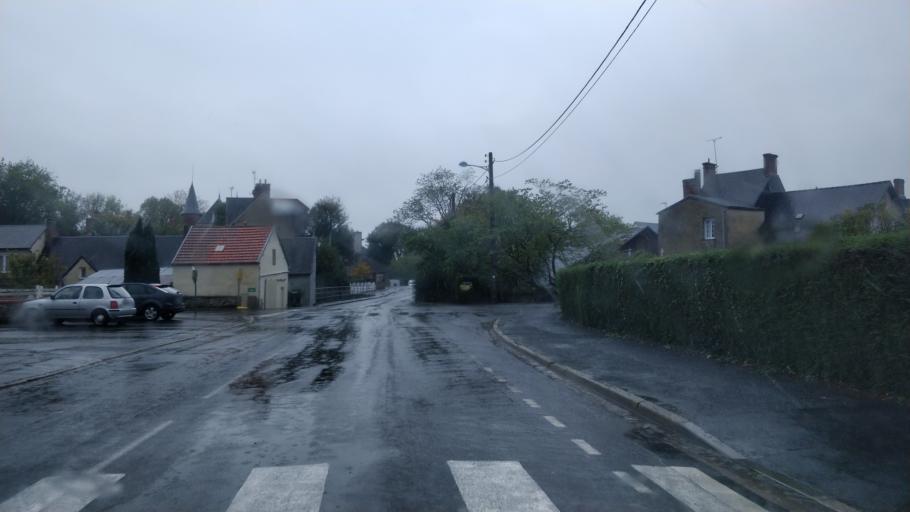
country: FR
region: Lower Normandy
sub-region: Departement de la Manche
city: Brehal
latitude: 48.8966
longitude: -1.5123
